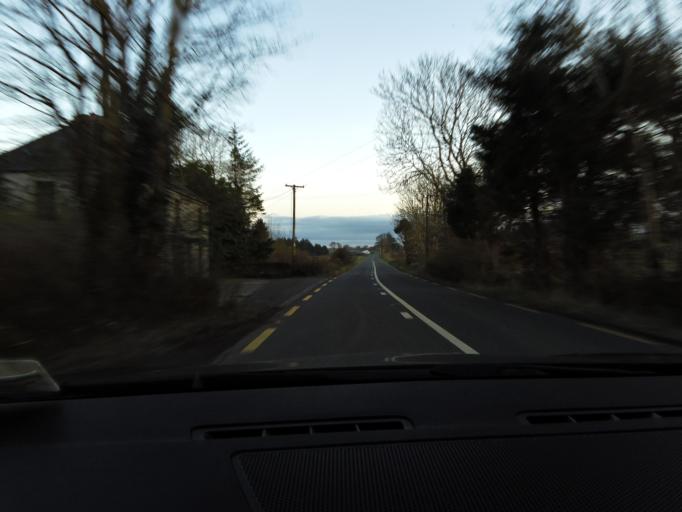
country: IE
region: Connaught
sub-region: Roscommon
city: Boyle
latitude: 53.9291
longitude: -8.2773
